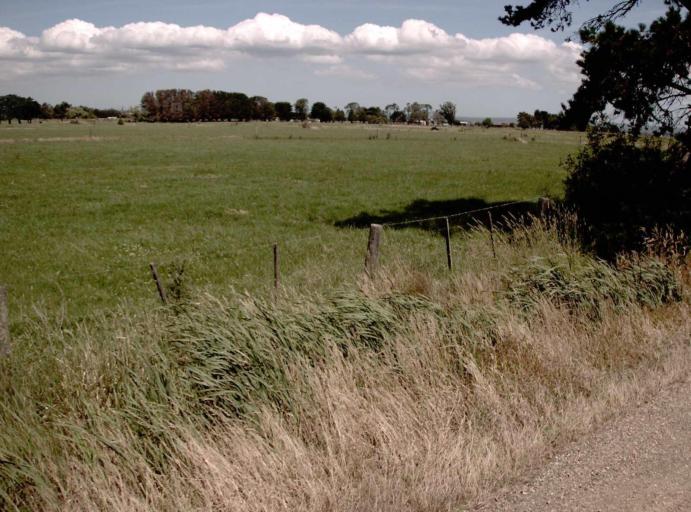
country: AU
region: Victoria
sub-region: Wellington
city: Heyfield
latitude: -38.0677
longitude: 146.8713
